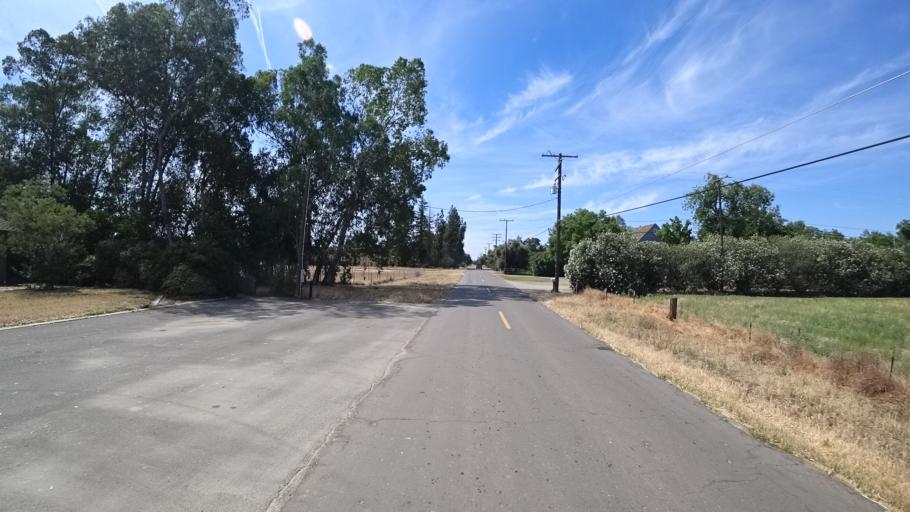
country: US
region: California
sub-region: Kings County
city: Hanford
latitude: 36.3556
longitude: -119.6222
